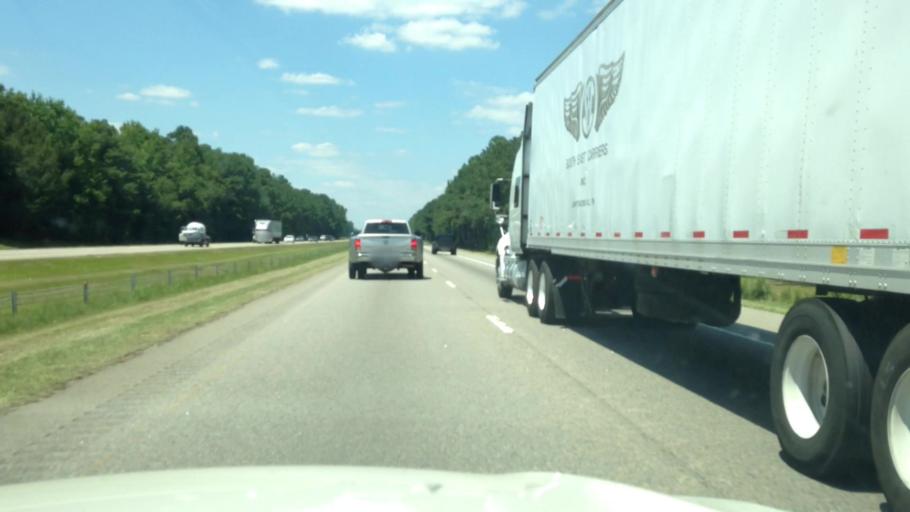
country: US
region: North Carolina
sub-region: Robeson County
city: Saint Pauls
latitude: 34.7755
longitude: -78.9957
